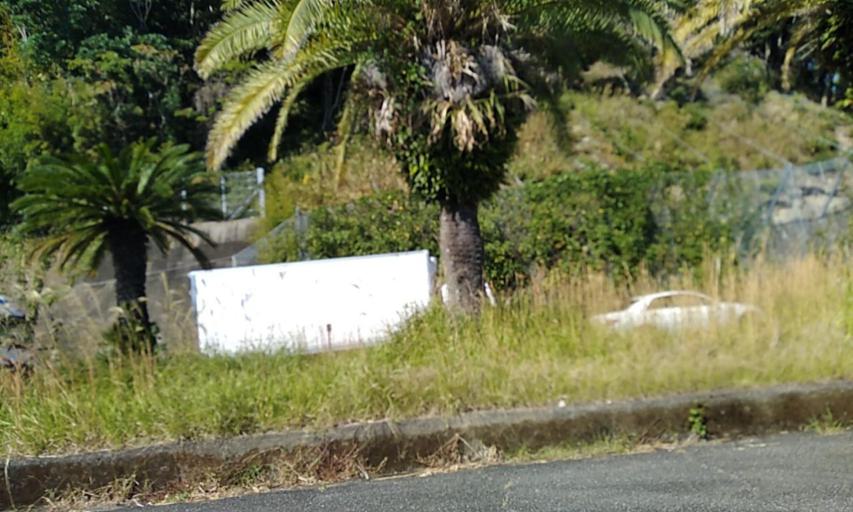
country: JP
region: Wakayama
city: Shingu
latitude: 33.8837
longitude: 136.0976
